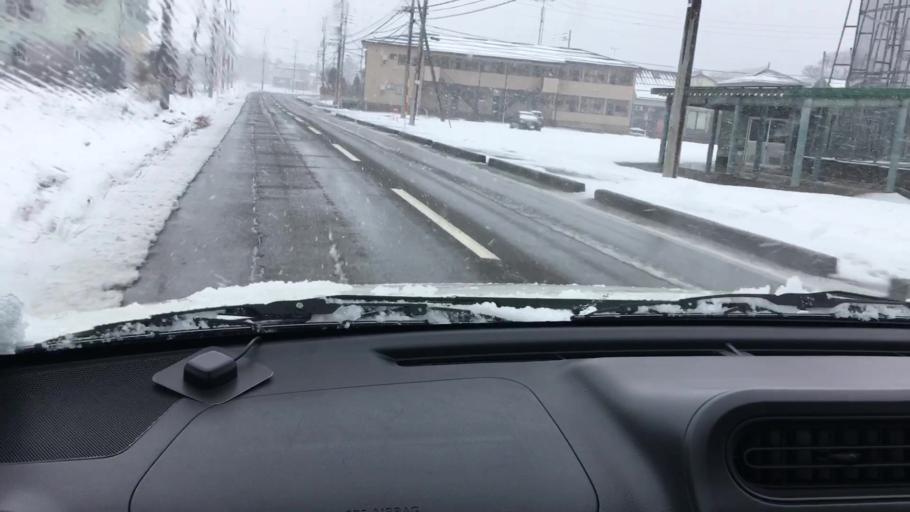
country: JP
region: Niigata
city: Joetsu
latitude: 37.0825
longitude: 138.2418
